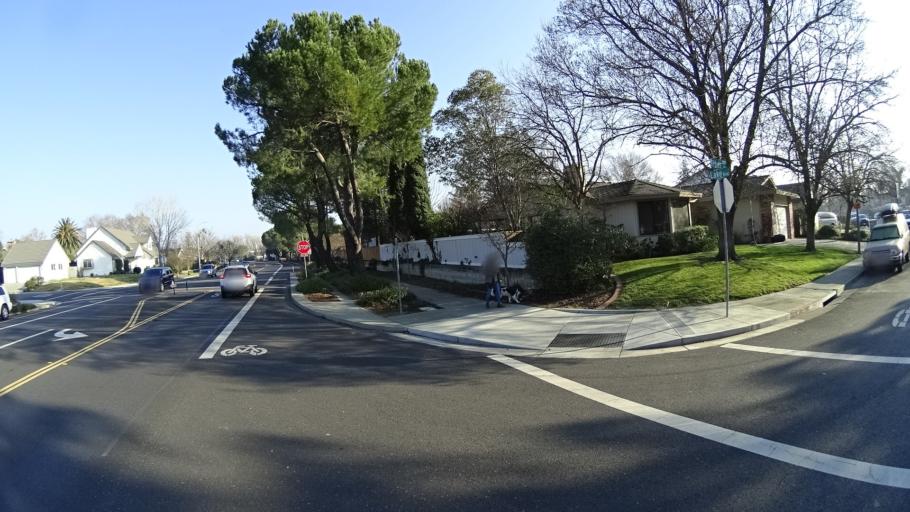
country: US
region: California
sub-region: Yolo County
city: Davis
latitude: 38.5569
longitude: -121.7873
